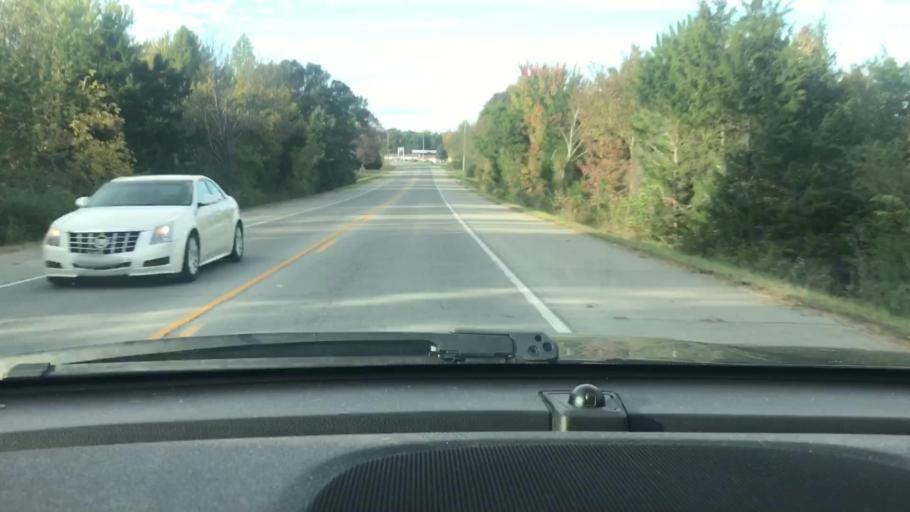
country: US
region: Tennessee
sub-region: Dickson County
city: White Bluff
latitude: 36.1224
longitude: -87.2269
